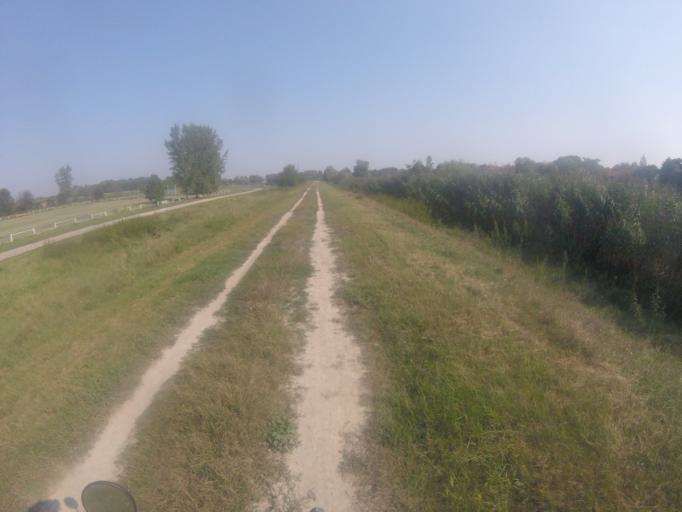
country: HU
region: Bacs-Kiskun
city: Baja
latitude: 46.2050
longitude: 18.9551
